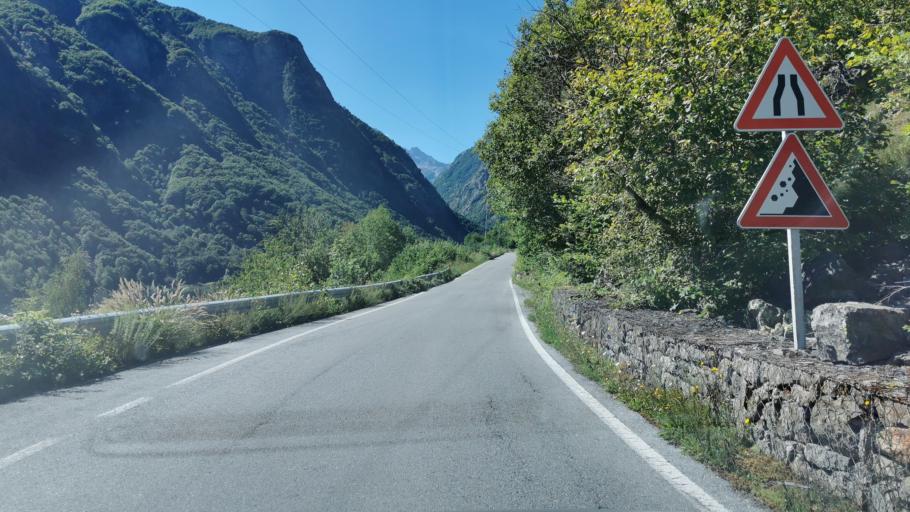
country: IT
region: Piedmont
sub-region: Provincia di Cuneo
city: Entracque
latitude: 44.2237
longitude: 7.3872
